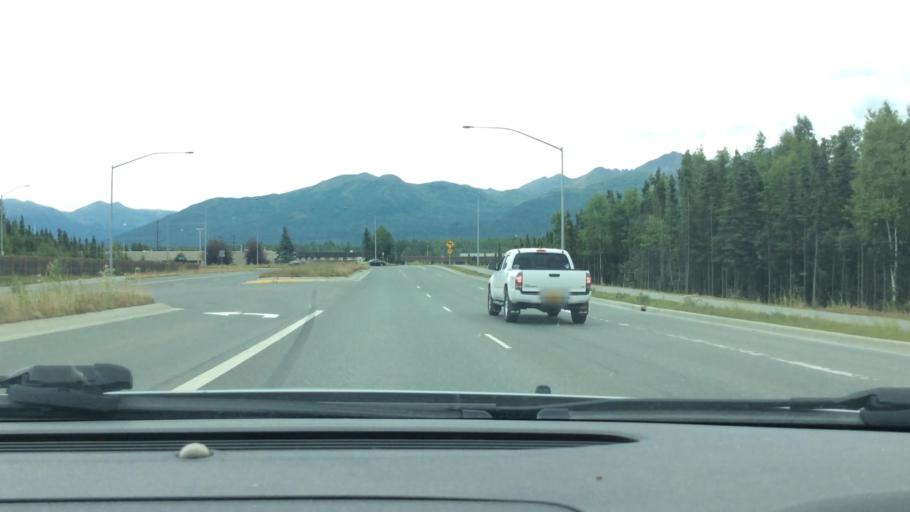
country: US
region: Alaska
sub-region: Anchorage Municipality
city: Anchorage
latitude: 61.1787
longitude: -149.7826
